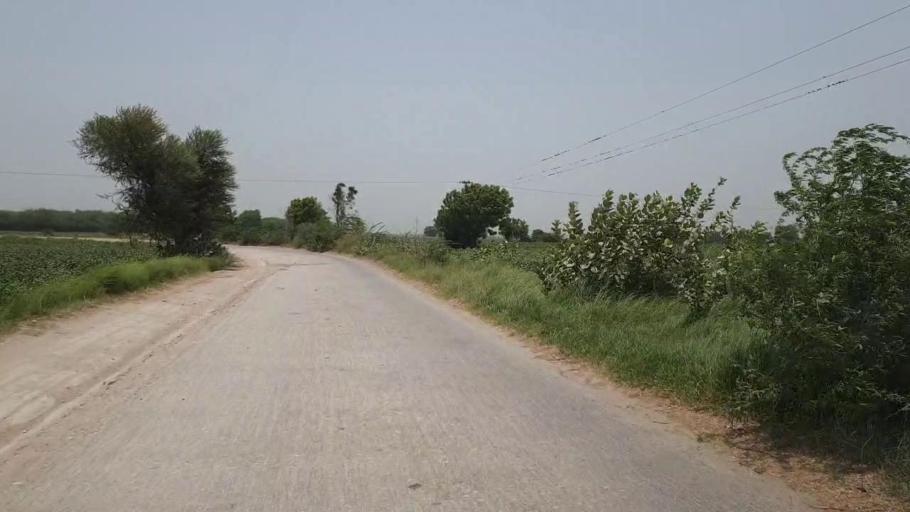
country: PK
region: Sindh
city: Tando Mittha Khan
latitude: 26.0677
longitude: 69.2016
